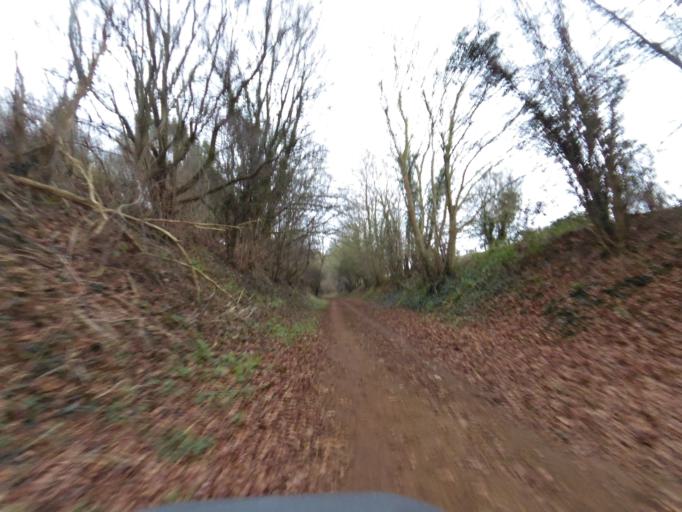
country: GB
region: England
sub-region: Norfolk
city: Costessey
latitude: 52.7129
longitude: 1.1526
